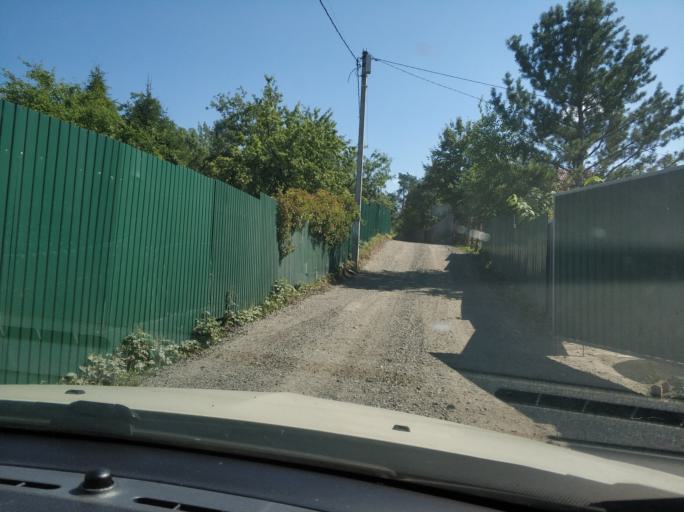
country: RU
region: Leningrad
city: Osel'ki
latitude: 60.2247
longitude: 30.5619
